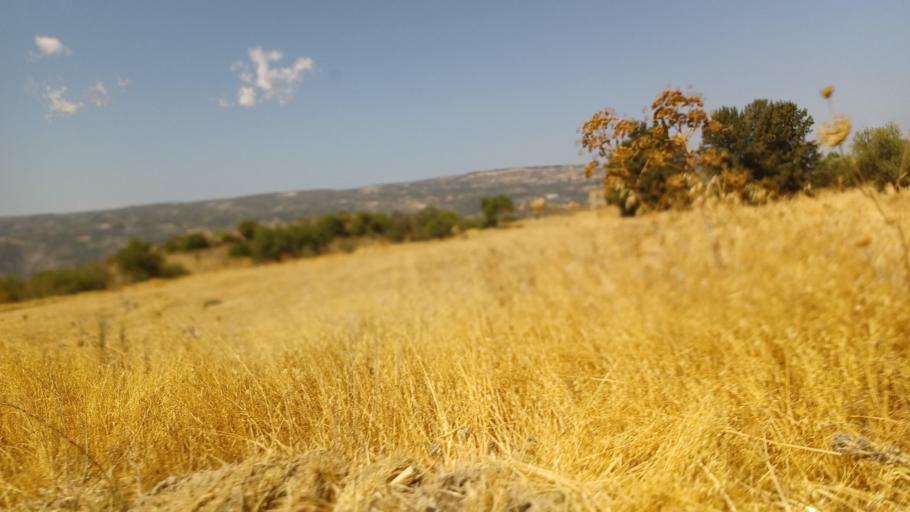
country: CY
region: Pafos
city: Polis
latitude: 34.9731
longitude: 32.4887
